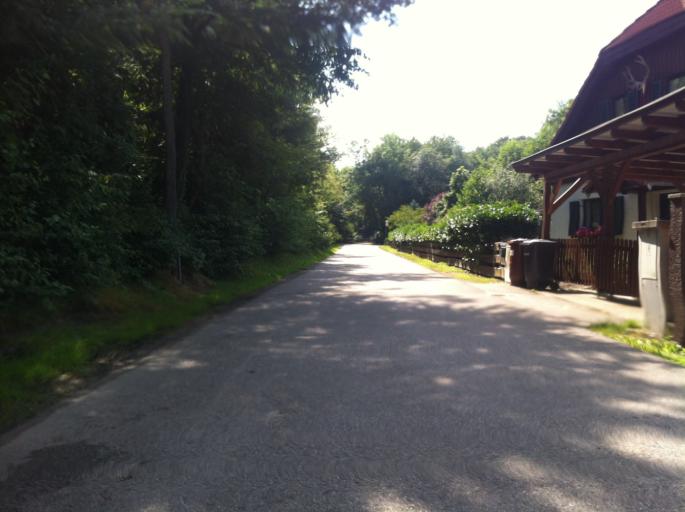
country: AT
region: Lower Austria
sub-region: Politischer Bezirk Modling
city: Laab im Walde
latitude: 48.1809
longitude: 16.1715
